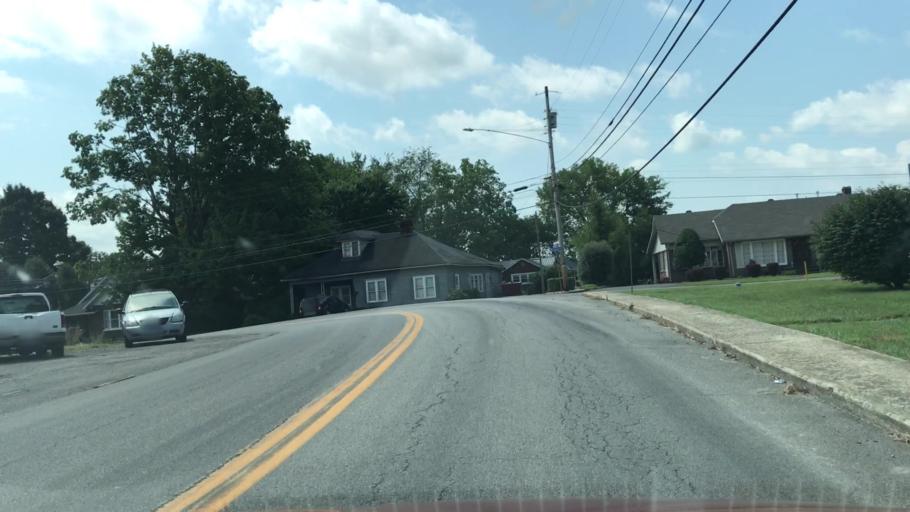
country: US
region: Kentucky
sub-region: Monroe County
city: Tompkinsville
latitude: 36.7054
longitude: -85.6994
